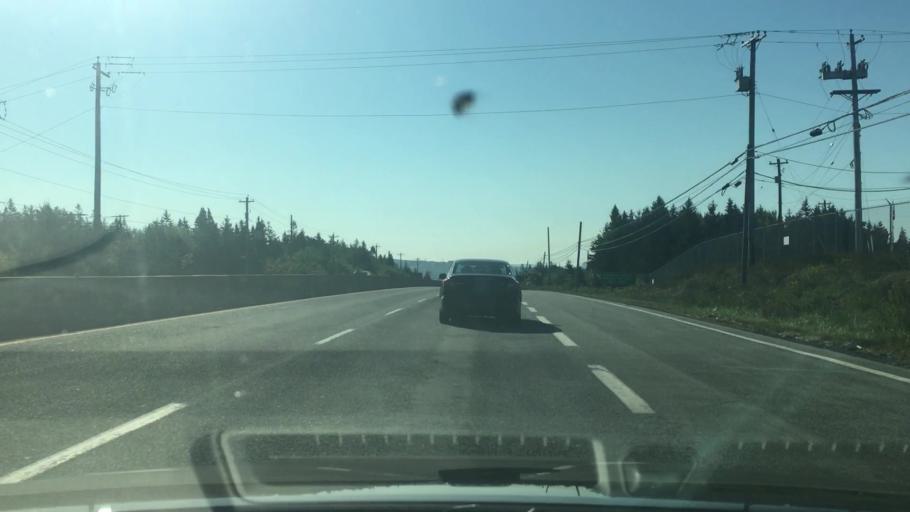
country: CA
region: Nova Scotia
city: Dartmouth
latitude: 44.7184
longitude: -63.6356
